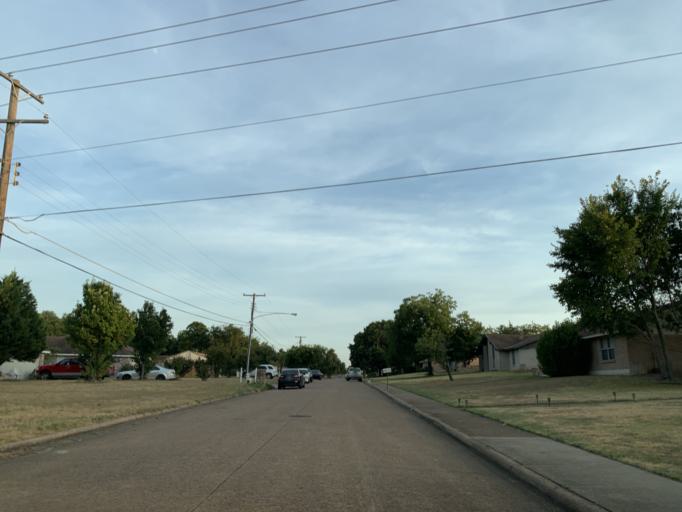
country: US
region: Texas
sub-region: Dallas County
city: Cockrell Hill
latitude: 32.7034
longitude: -96.8872
